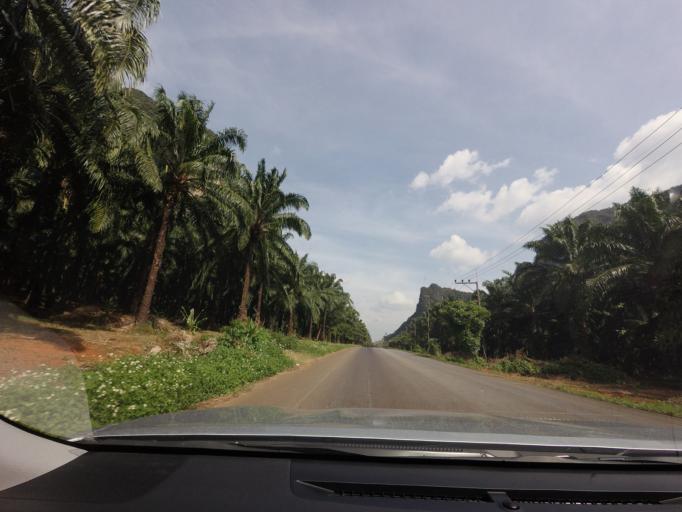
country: TH
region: Phangnga
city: Ban Ao Nang
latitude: 8.1462
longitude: 98.8165
